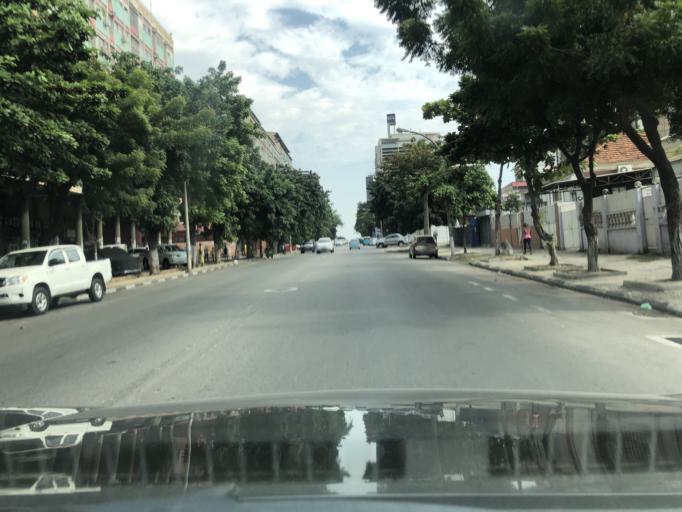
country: AO
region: Luanda
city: Luanda
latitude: -8.8205
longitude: 13.2303
